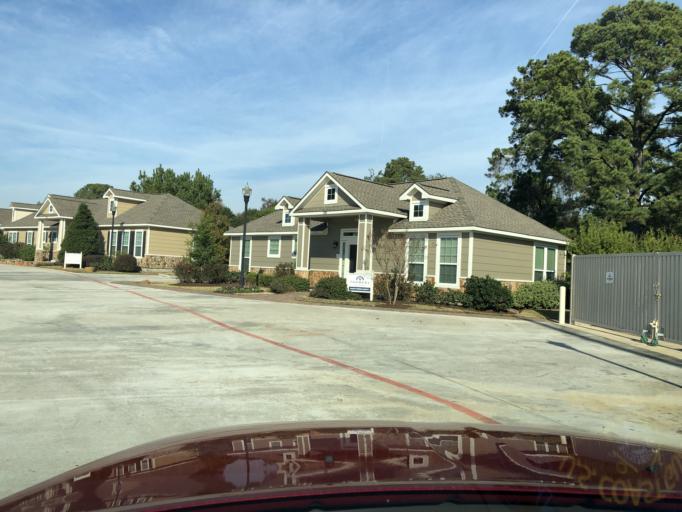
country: US
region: Texas
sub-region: Harris County
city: Tomball
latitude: 30.0358
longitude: -95.5569
